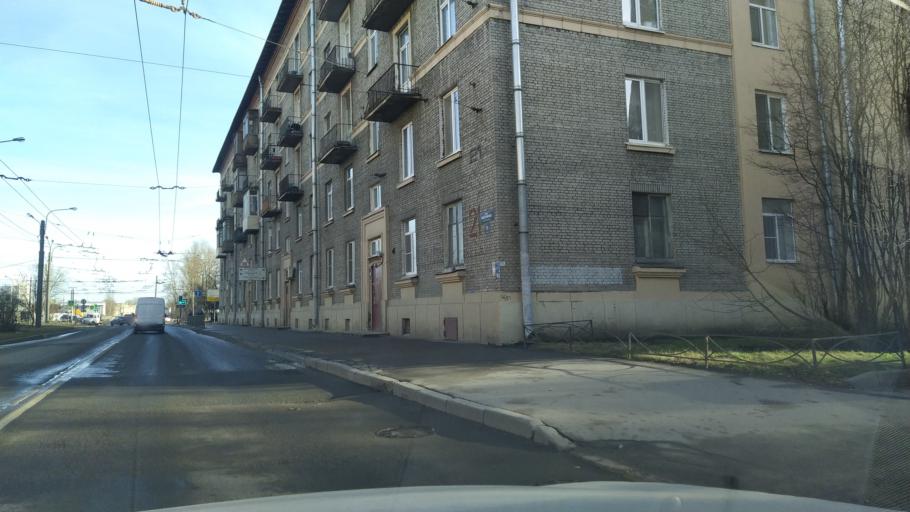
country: RU
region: St.-Petersburg
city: Kupchino
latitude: 59.8788
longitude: 30.3343
